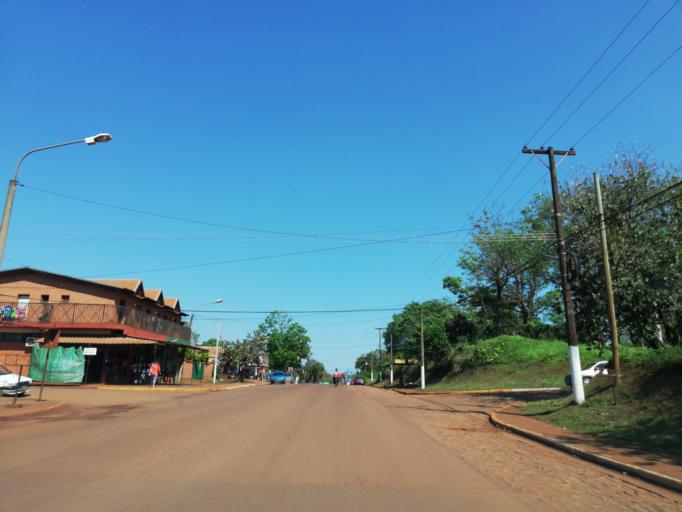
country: AR
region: Misiones
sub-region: Departamento de Eldorado
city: Eldorado
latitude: -26.4066
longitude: -54.6553
